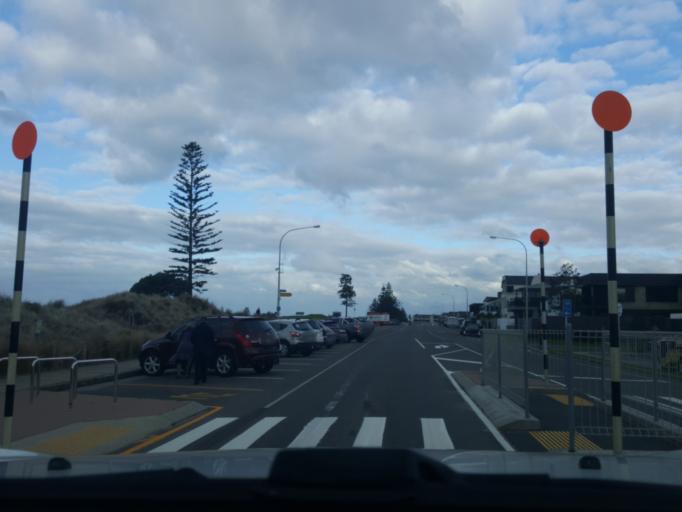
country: NZ
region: Bay of Plenty
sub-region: Tauranga City
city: Tauranga
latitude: -37.6467
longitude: 176.1984
